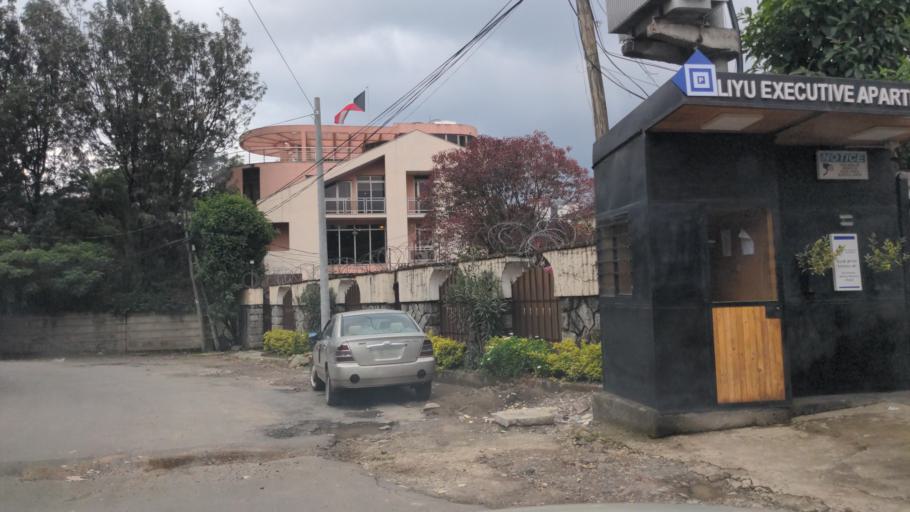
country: ET
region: Adis Abeba
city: Addis Ababa
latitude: 8.9957
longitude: 38.7781
